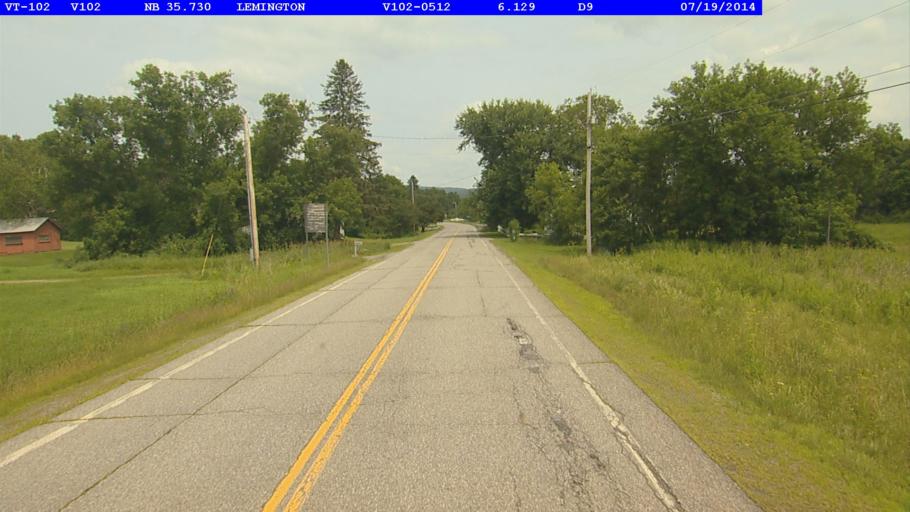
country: US
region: New Hampshire
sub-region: Coos County
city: Colebrook
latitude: 44.8969
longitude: -71.5101
